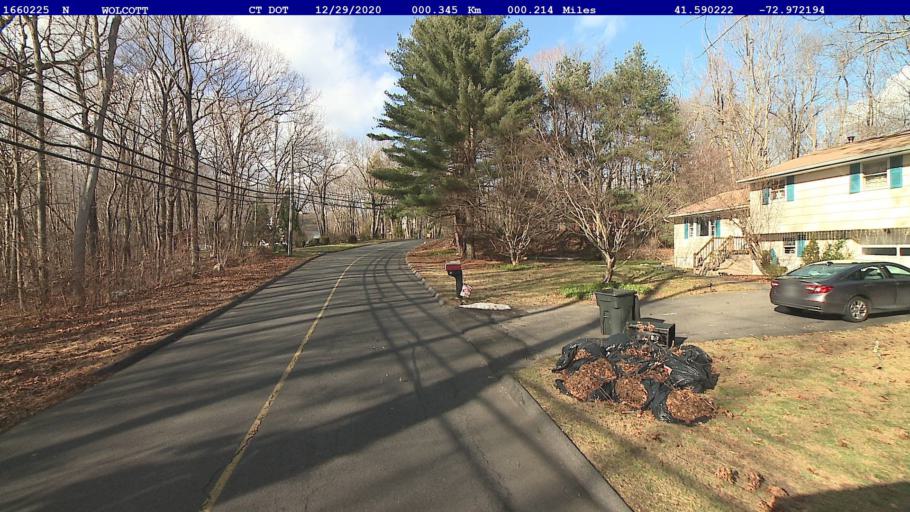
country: US
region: Connecticut
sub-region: New Haven County
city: Wolcott
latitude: 41.5902
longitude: -72.9722
